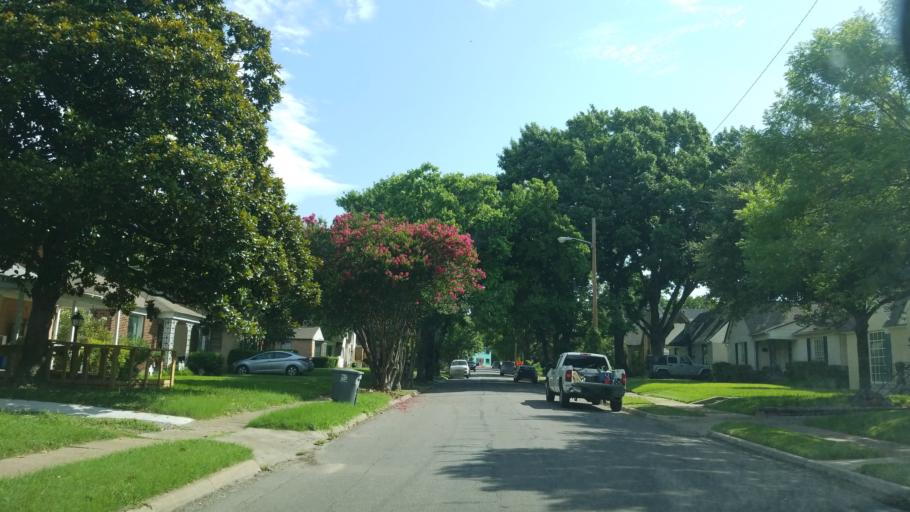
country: US
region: Texas
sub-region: Dallas County
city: Highland Park
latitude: 32.8169
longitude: -96.7838
